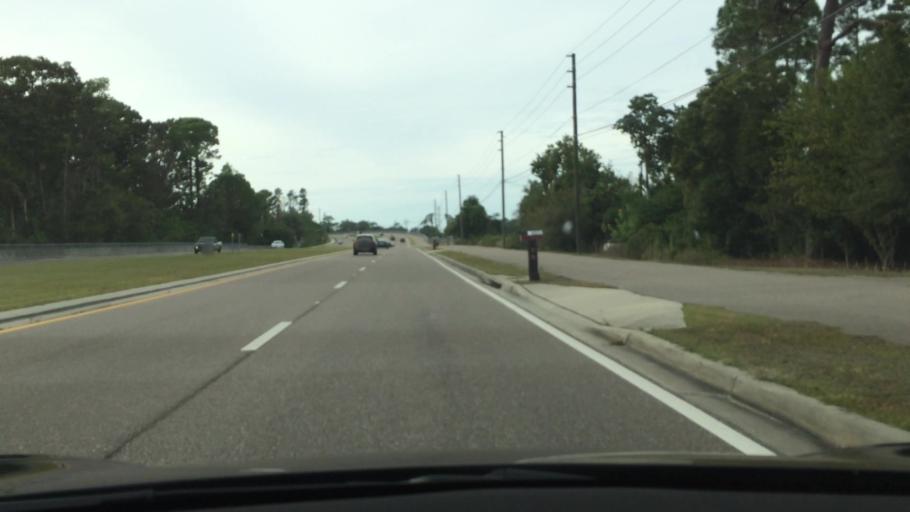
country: US
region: Florida
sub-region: Pinellas County
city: Tarpon Springs
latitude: 28.1527
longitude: -82.7182
